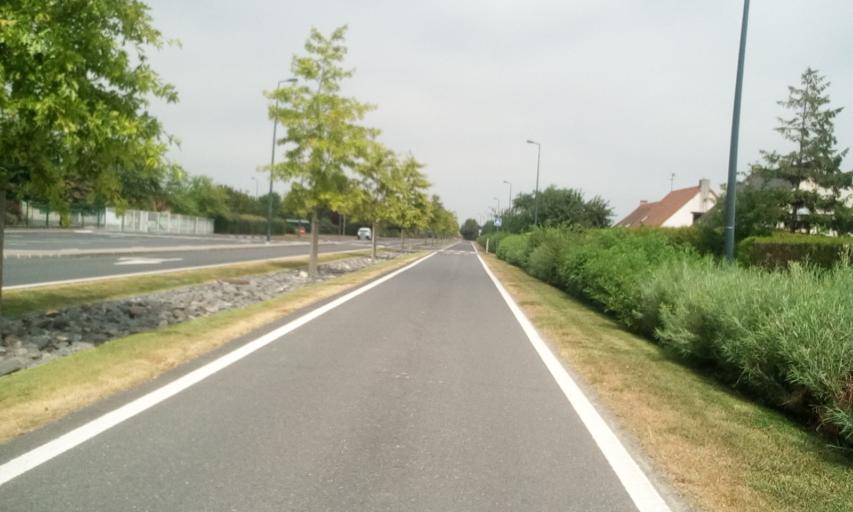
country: FR
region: Lower Normandy
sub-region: Departement du Calvados
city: Douvres-la-Delivrande
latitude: 49.2974
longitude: -0.3874
